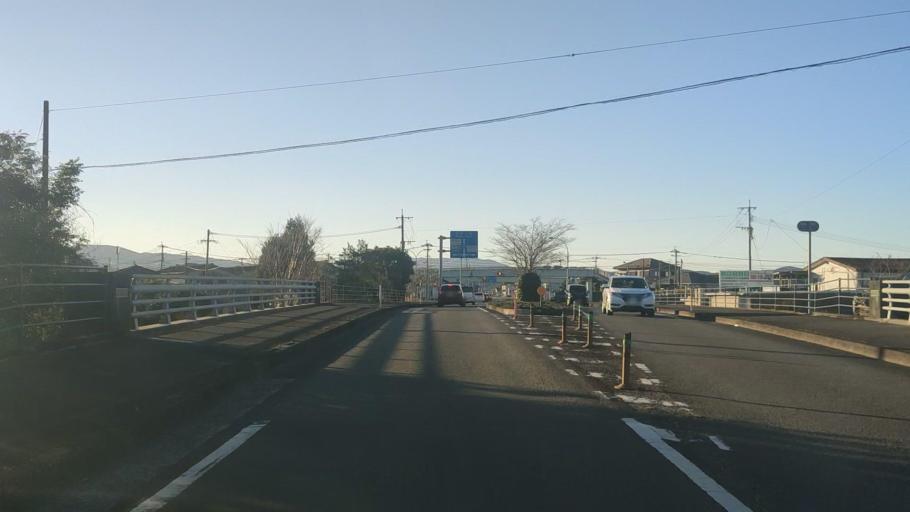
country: JP
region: Miyazaki
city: Miyazaki-shi
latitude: 31.8318
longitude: 131.3014
